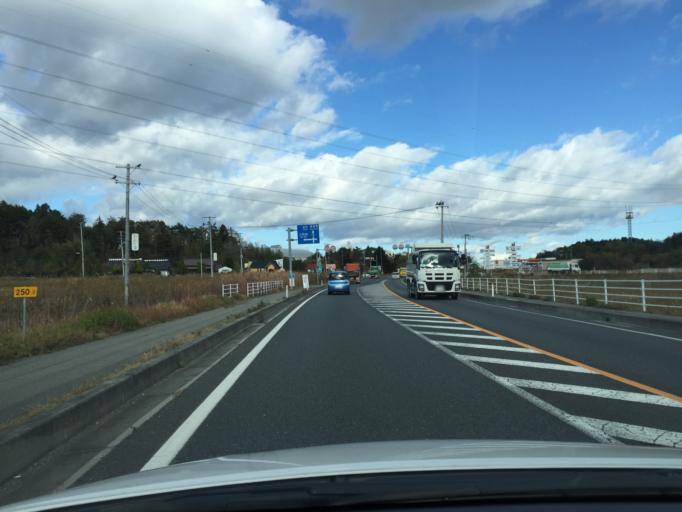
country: JP
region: Fukushima
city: Namie
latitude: 37.4058
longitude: 140.9975
